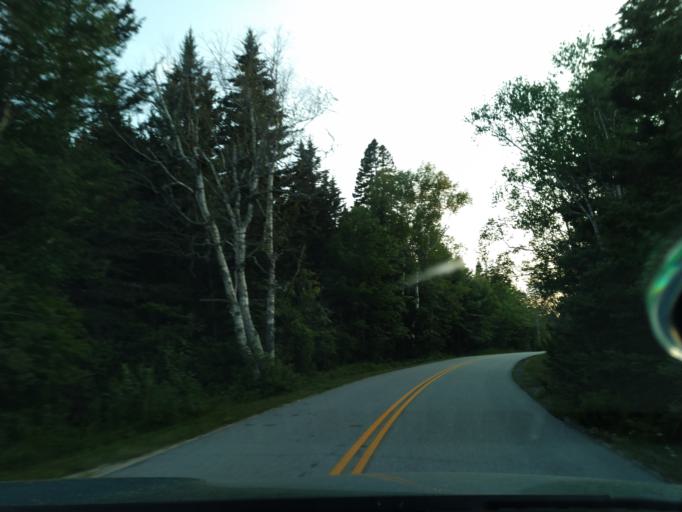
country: US
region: Maine
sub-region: Hancock County
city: Gouldsboro
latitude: 44.3742
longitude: -68.0716
